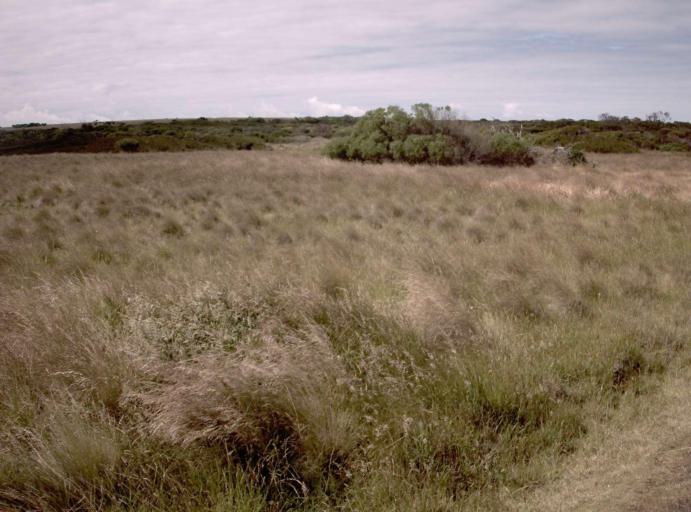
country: AU
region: Victoria
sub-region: Bass Coast
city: Phillip Island
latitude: -38.5068
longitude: 145.1400
